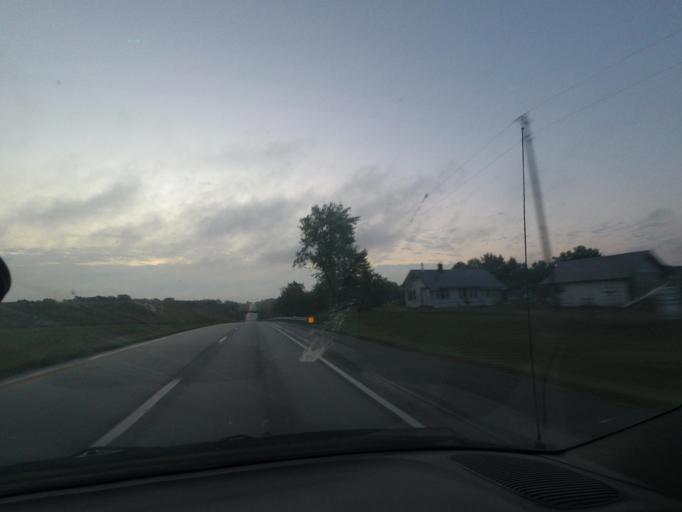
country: US
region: Missouri
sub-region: Linn County
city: Marceline
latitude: 39.7600
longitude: -92.9134
